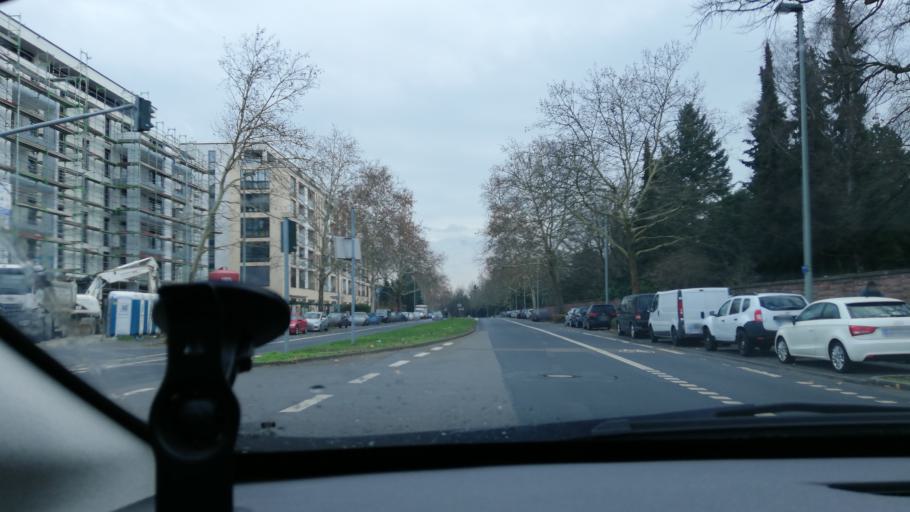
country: DE
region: Hesse
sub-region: Regierungsbezirk Darmstadt
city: Frankfurt am Main
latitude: 50.1392
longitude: 8.6941
